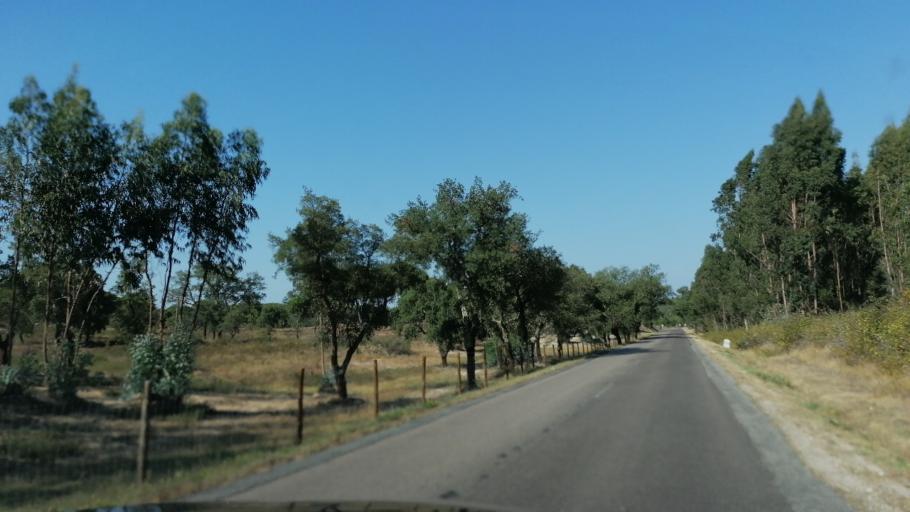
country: PT
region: Evora
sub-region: Vendas Novas
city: Vendas Novas
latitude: 38.7821
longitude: -8.5868
